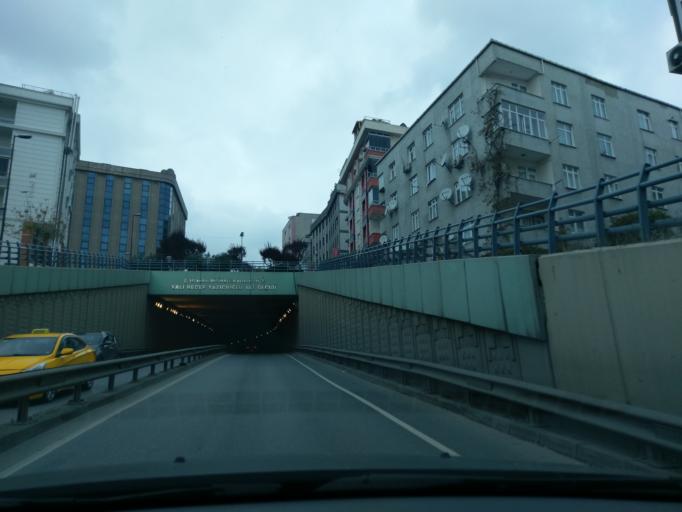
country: TR
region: Istanbul
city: Bahcelievler
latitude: 41.0140
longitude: 28.8439
